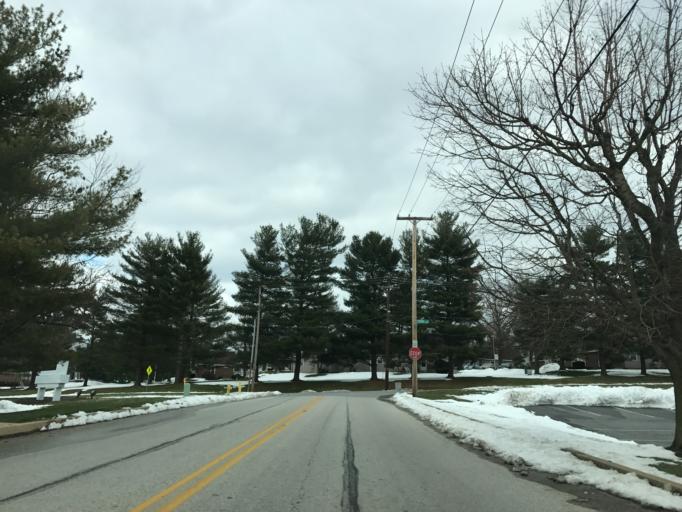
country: US
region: Pennsylvania
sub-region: York County
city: North York
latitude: 39.9852
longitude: -76.7466
